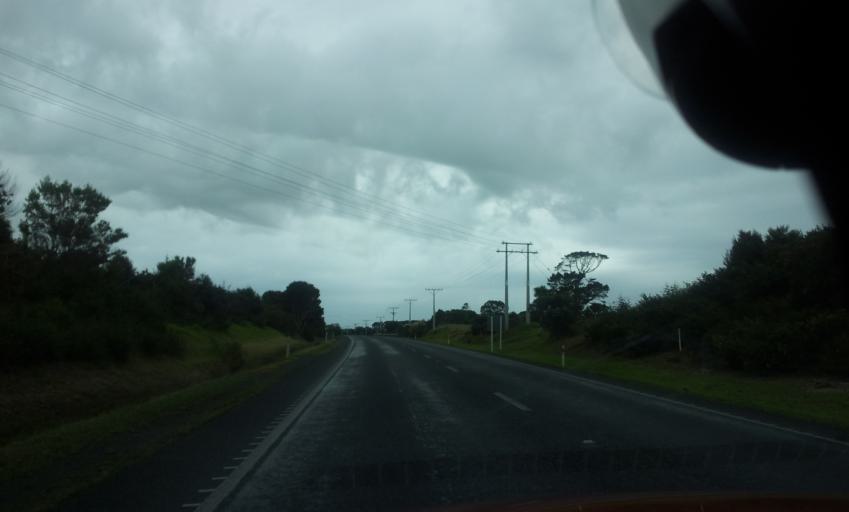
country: NZ
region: Northland
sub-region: Whangarei
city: Ruakaka
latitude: -35.9176
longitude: 174.4525
